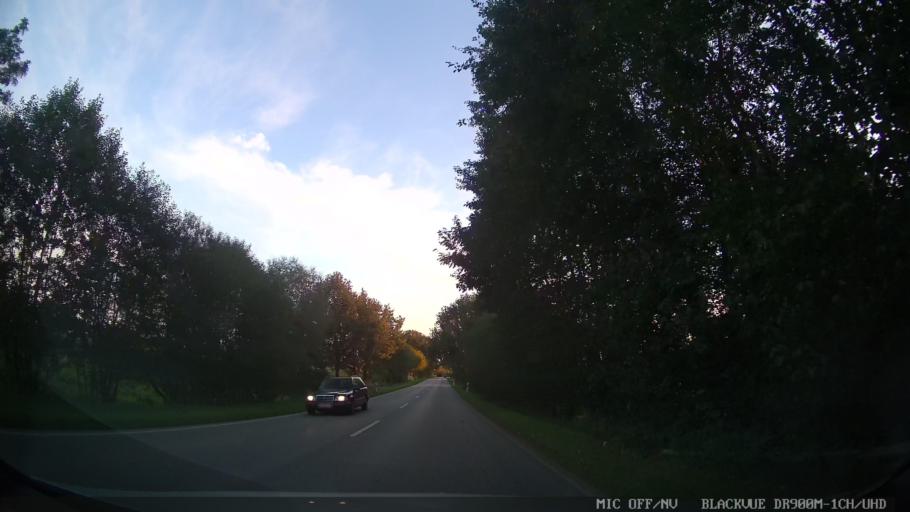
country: DE
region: Schleswig-Holstein
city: Susel
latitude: 54.0711
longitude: 10.6874
